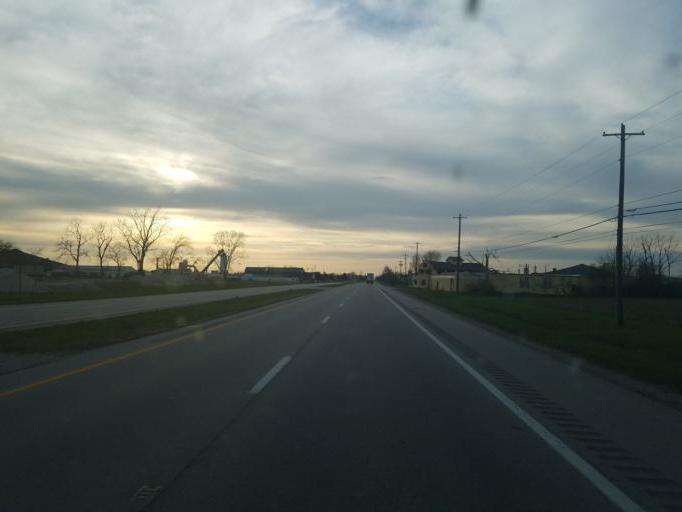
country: US
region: Ohio
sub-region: Sandusky County
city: Woodville
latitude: 41.4427
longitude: -83.3439
